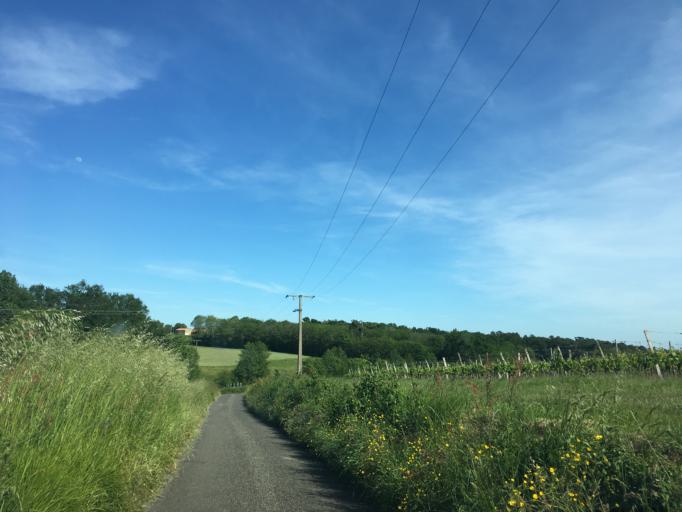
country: FR
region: Poitou-Charentes
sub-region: Departement de la Charente-Maritime
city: Mirambeau
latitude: 45.3377
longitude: -0.5874
